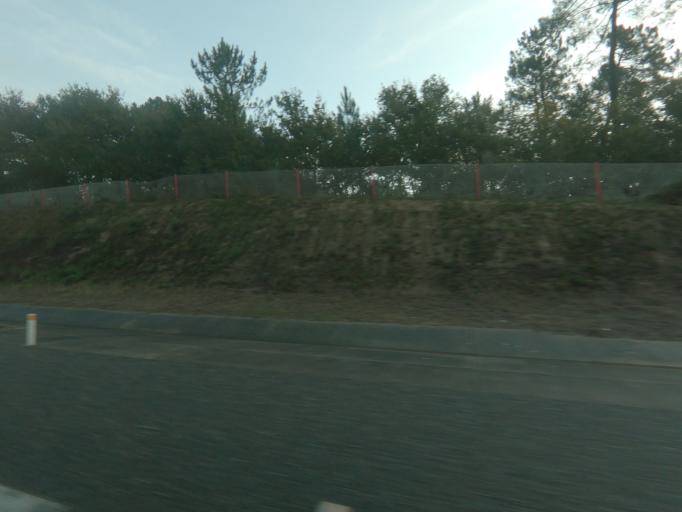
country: ES
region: Galicia
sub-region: Provincia de Pontevedra
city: Tui
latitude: 42.0940
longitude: -8.6434
